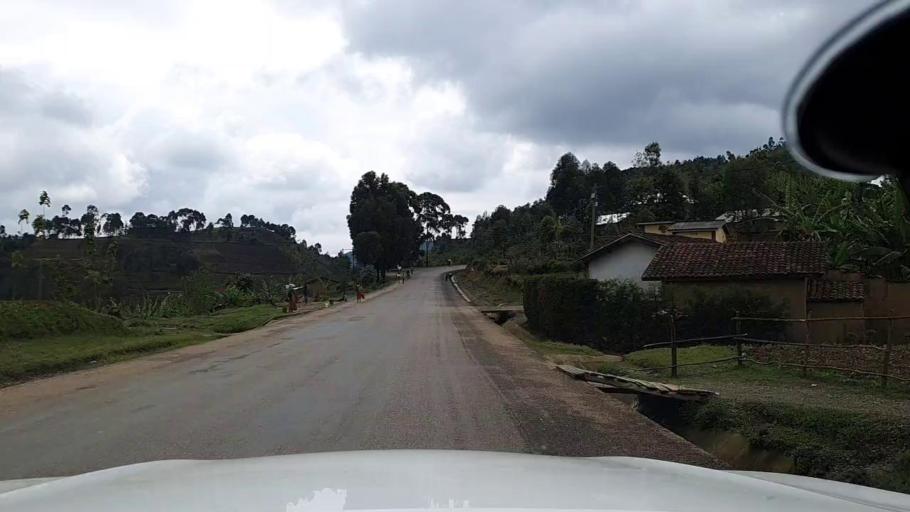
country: RW
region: Western Province
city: Kibuye
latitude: -2.0631
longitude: 29.5349
